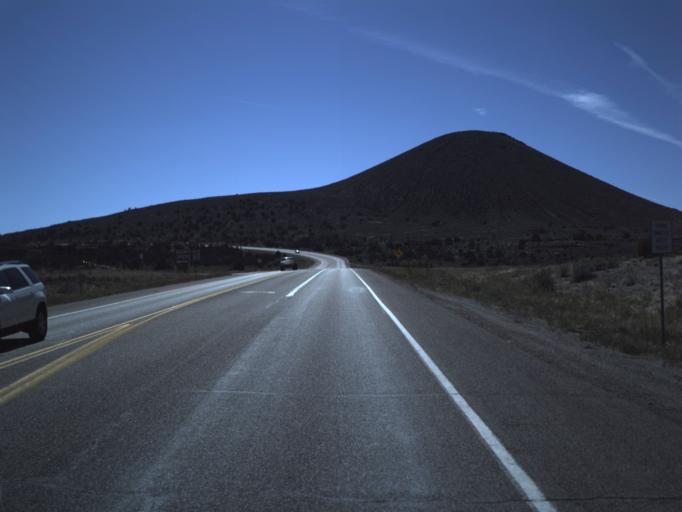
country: US
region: Utah
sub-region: Washington County
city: Ivins
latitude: 37.3304
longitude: -113.6933
